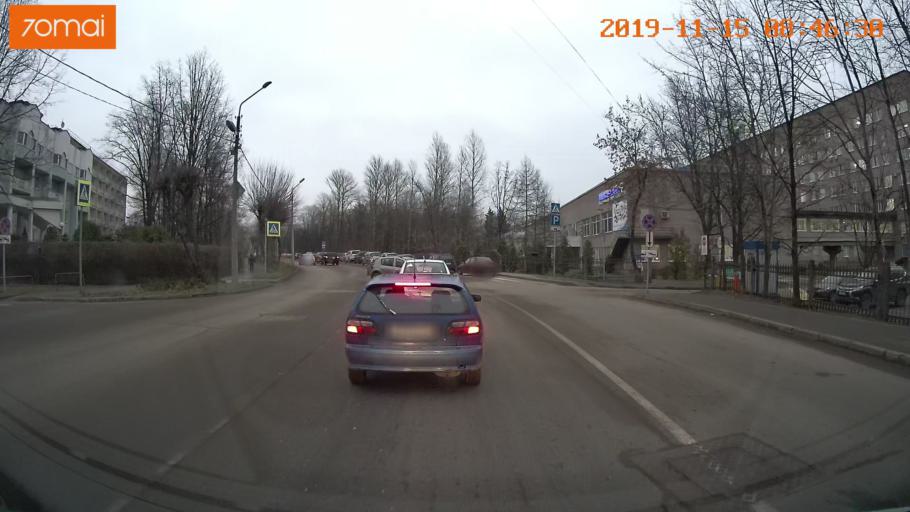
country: RU
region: Vologda
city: Cherepovets
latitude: 59.1187
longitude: 37.9067
